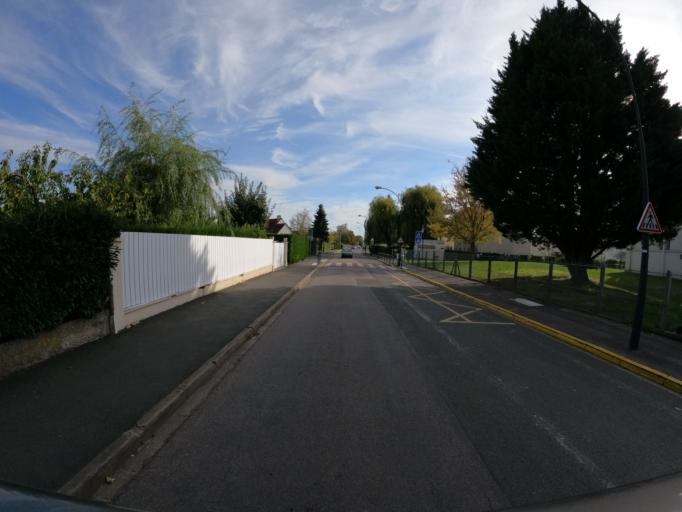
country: FR
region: Ile-de-France
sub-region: Departement de Seine-et-Marne
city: Pontault-Combault
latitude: 48.7886
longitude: 2.5972
